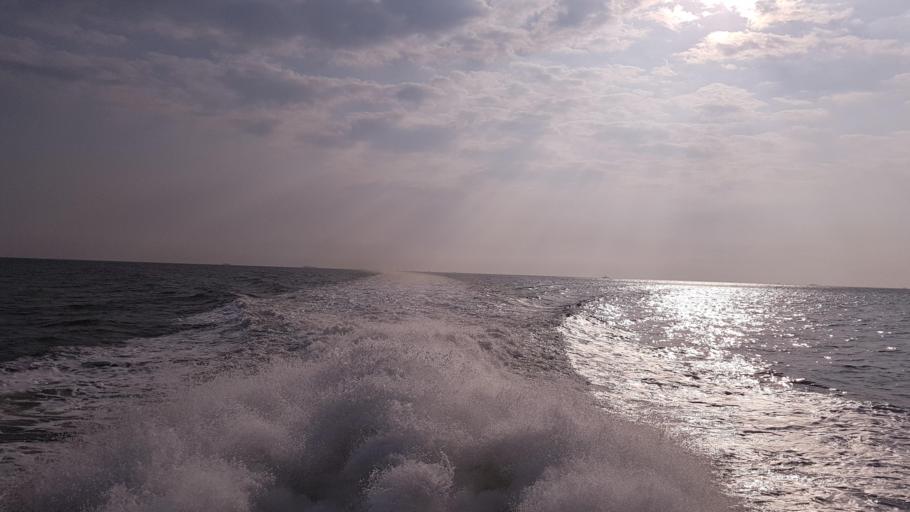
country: DE
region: Schleswig-Holstein
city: Grode
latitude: 54.6090
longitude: 8.6824
